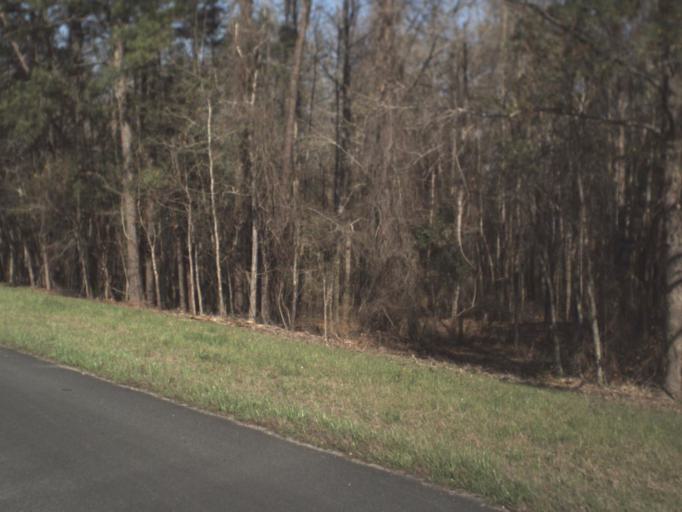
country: US
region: Florida
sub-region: Leon County
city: Tallahassee
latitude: 30.4985
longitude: -84.1906
